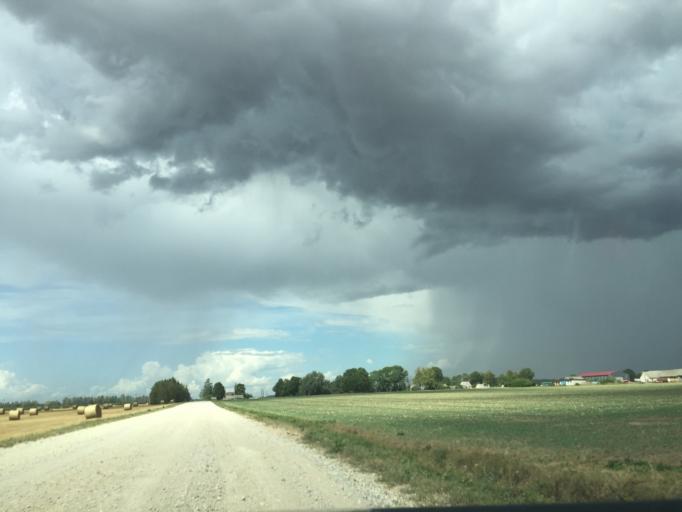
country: LT
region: Siauliu apskritis
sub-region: Joniskis
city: Joniskis
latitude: 56.2814
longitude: 23.7268
